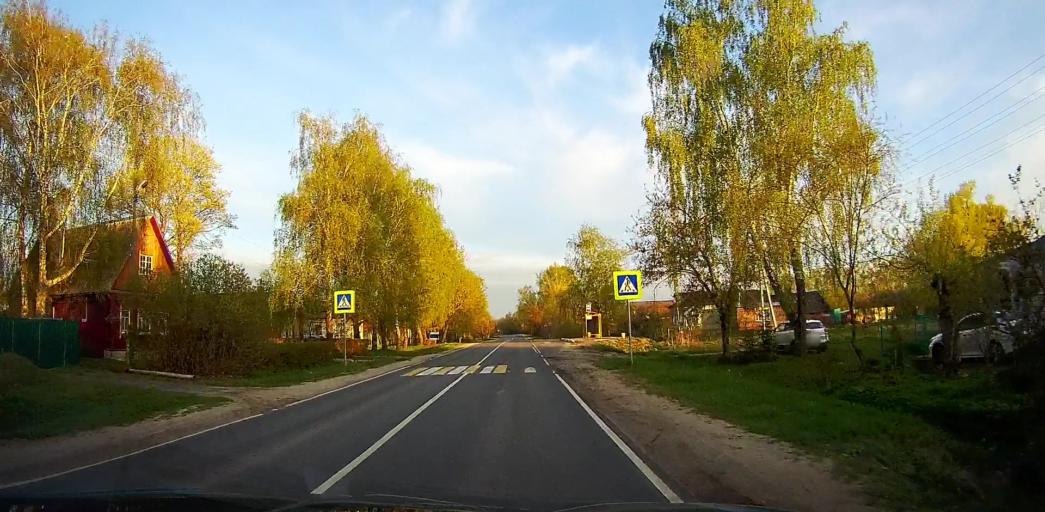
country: RU
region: Moskovskaya
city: Peski
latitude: 55.2125
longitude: 38.6735
